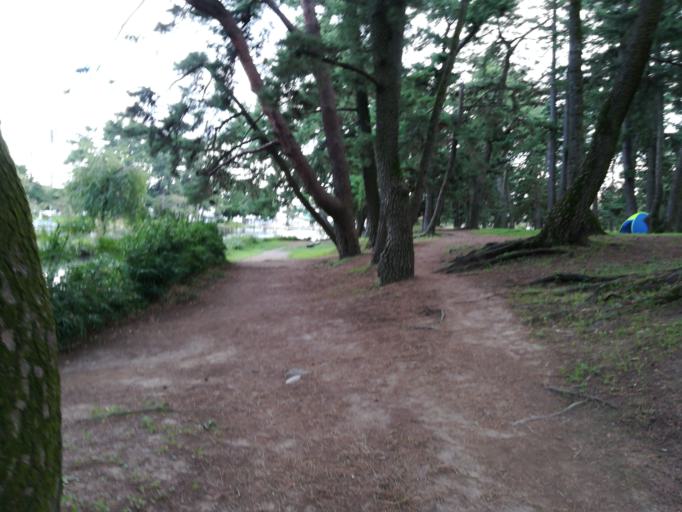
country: JP
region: Gunma
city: Maebashi-shi
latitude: 36.4169
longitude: 139.0515
